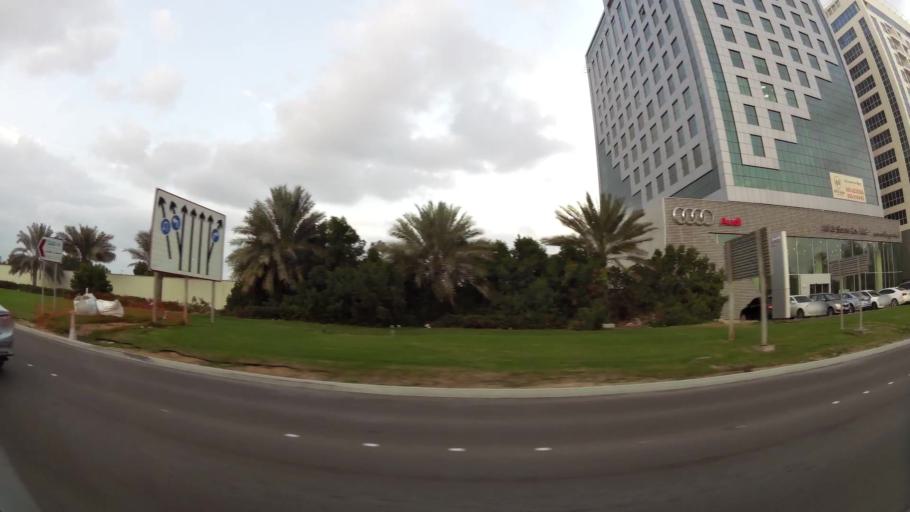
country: AE
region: Abu Dhabi
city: Abu Dhabi
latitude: 24.4205
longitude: 54.4595
